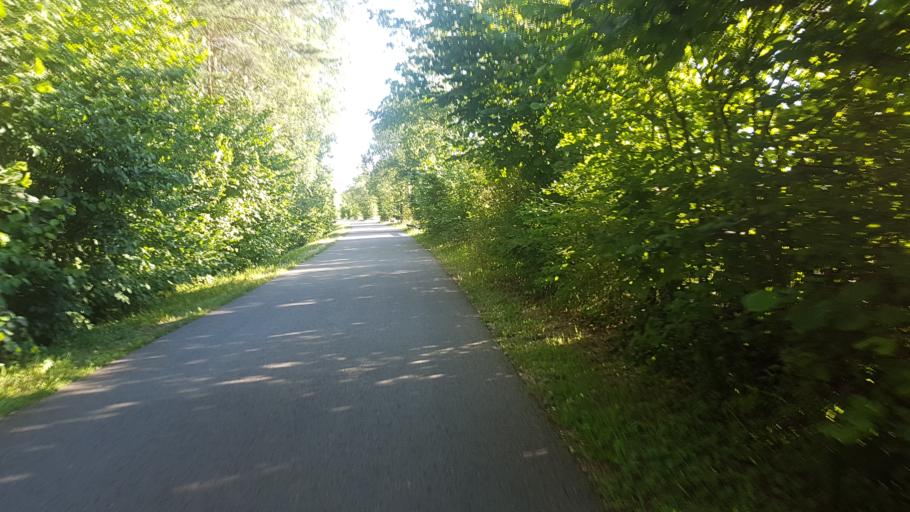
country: DE
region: Bavaria
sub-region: Regierungsbezirk Mittelfranken
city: Absberg
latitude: 49.1328
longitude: 10.8578
